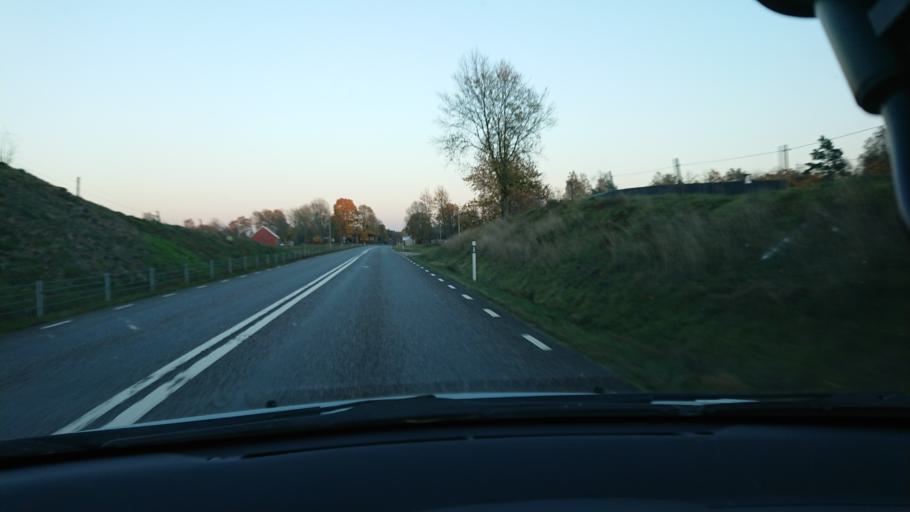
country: SE
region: Halland
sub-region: Laholms Kommun
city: Knared
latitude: 56.7144
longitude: 13.2416
